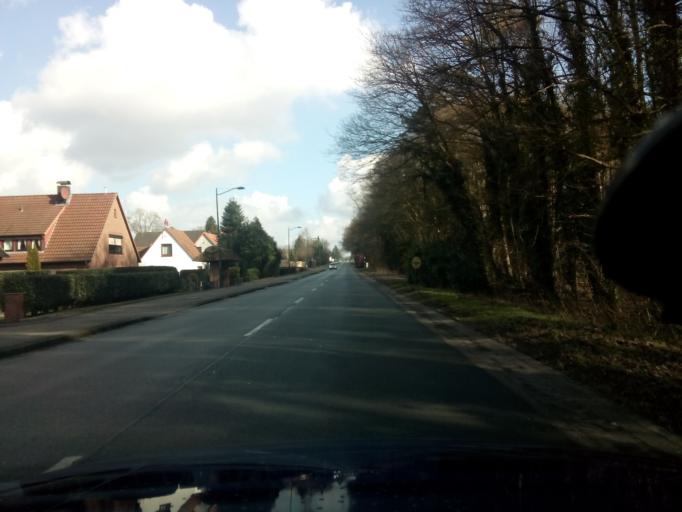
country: DE
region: Lower Saxony
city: Hambergen
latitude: 53.3147
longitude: 8.8608
